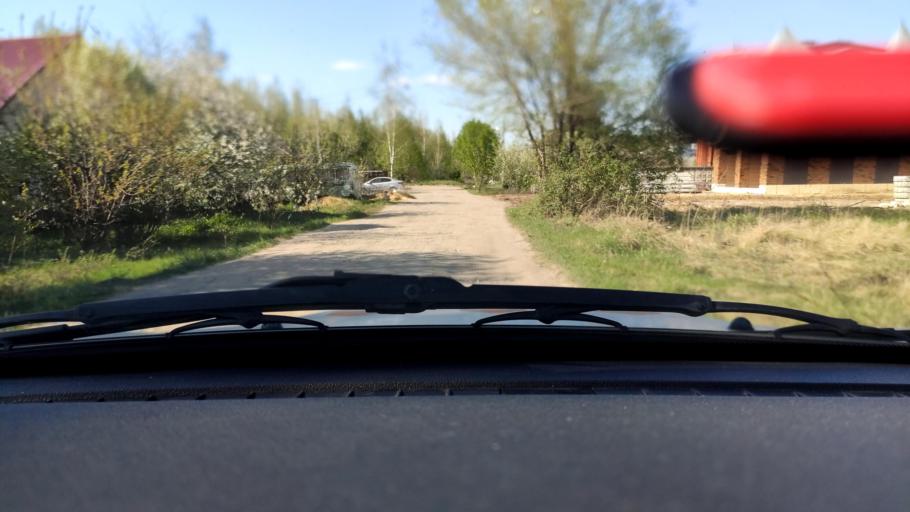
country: RU
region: Voronezj
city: Somovo
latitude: 51.6844
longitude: 39.3035
